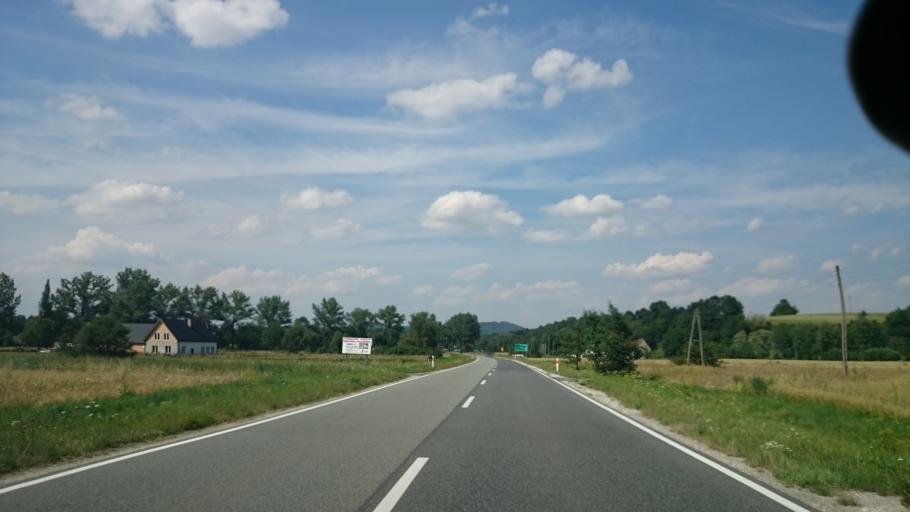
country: PL
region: Lower Silesian Voivodeship
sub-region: Powiat klodzki
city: Bystrzyca Klodzka
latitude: 50.3123
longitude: 16.6607
